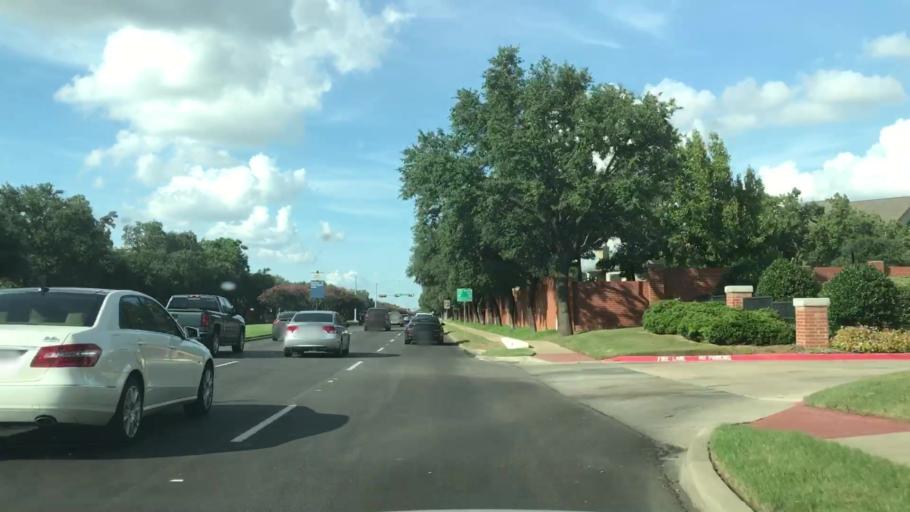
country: US
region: Texas
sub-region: Dallas County
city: Farmers Branch
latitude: 32.9285
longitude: -96.9520
